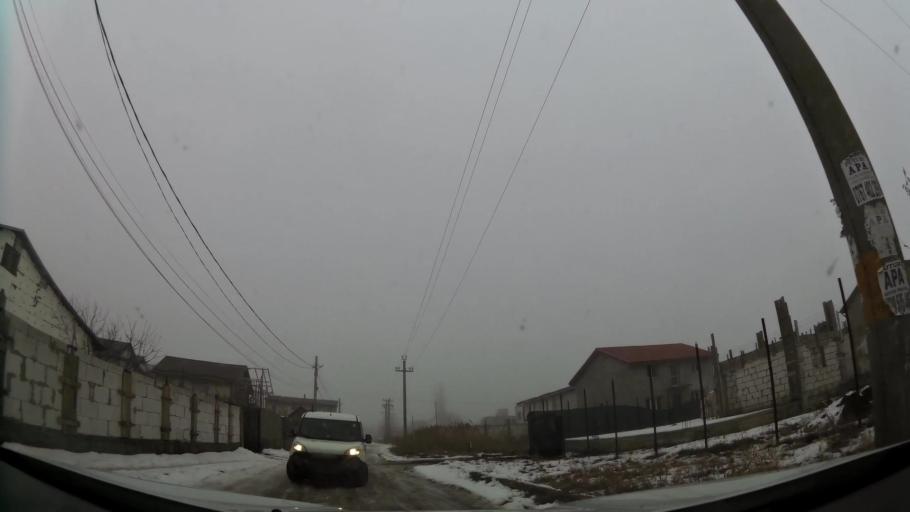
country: RO
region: Ilfov
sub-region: Comuna Chitila
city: Rudeni
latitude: 44.4684
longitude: 25.9806
